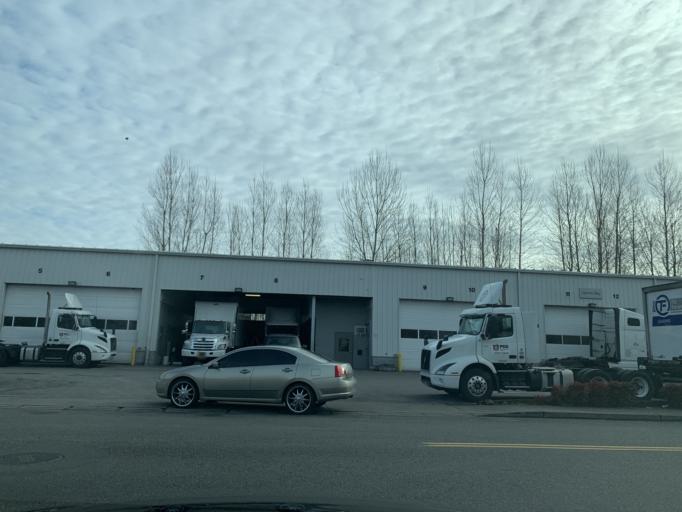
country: US
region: Washington
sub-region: Pierce County
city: Fife
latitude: 47.2440
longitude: -122.3500
